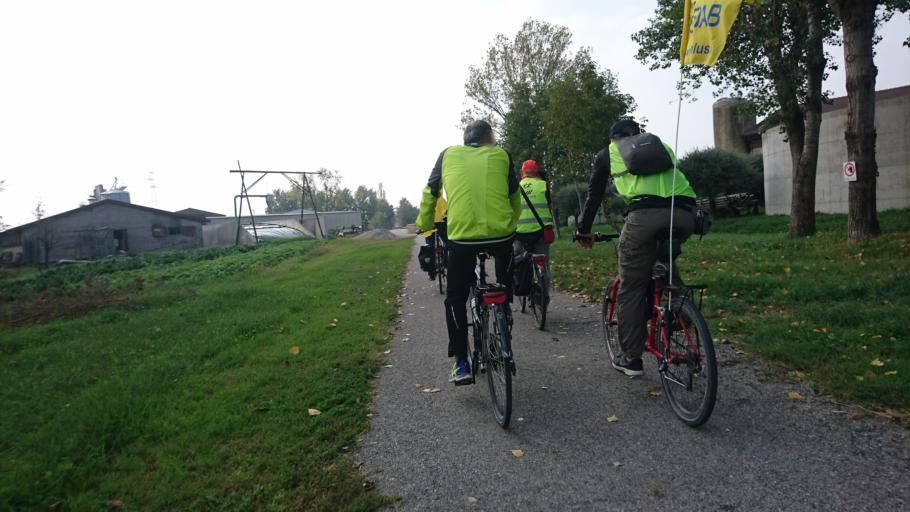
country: IT
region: Veneto
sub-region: Provincia di Padova
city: Piazzola sul Brenta
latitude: 45.5255
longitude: 11.7659
